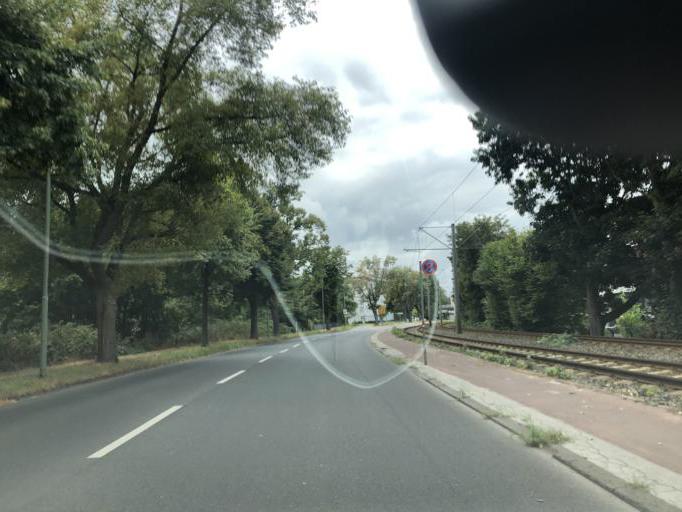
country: DE
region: North Rhine-Westphalia
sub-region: Regierungsbezirk Dusseldorf
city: Neuss
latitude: 51.1952
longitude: 6.7063
